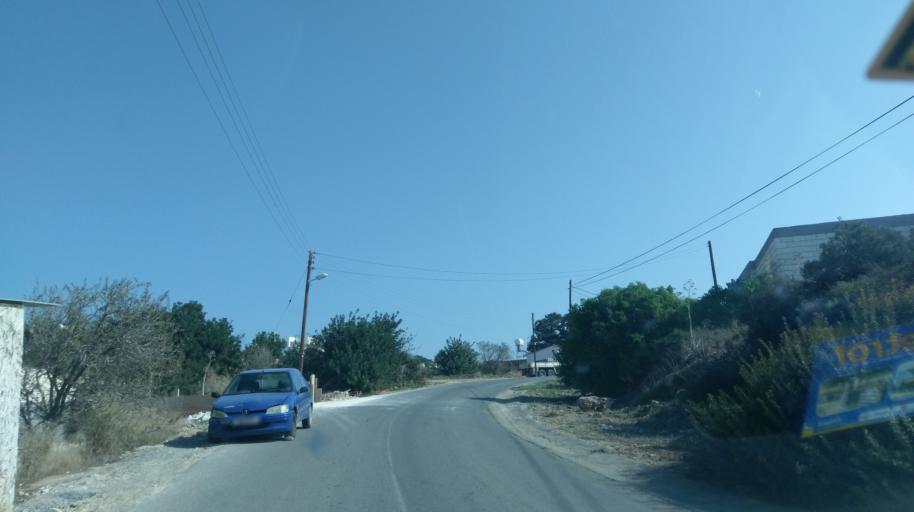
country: CY
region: Lefkosia
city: Morfou
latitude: 35.3414
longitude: 33.0152
